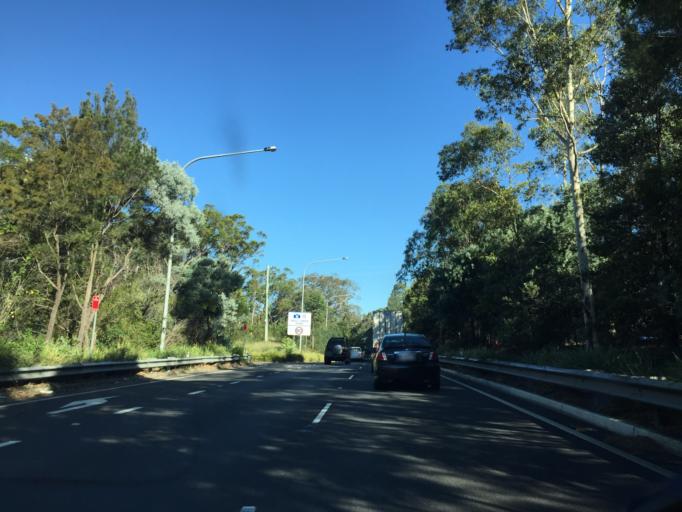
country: AU
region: New South Wales
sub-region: Blue Mountains Municipality
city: Blaxland
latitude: -33.7103
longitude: 150.5873
